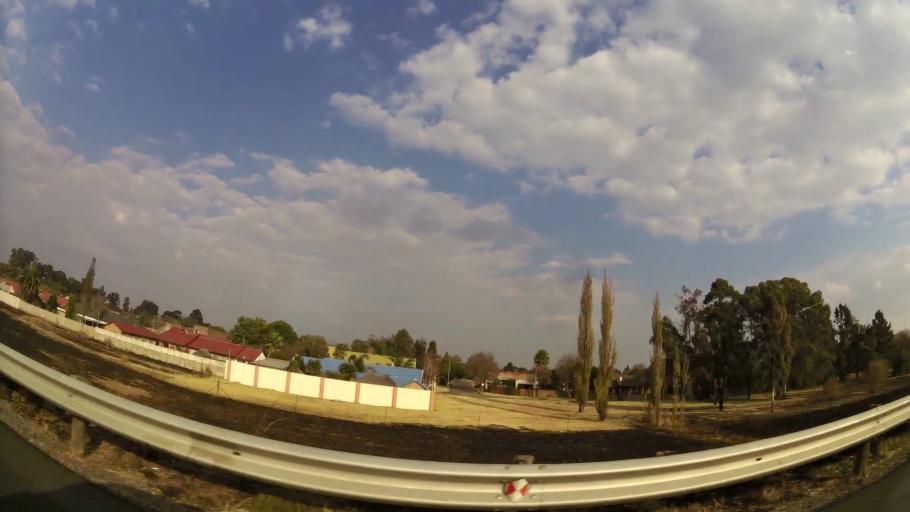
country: ZA
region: Gauteng
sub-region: Ekurhuleni Metropolitan Municipality
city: Springs
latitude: -26.2758
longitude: 28.4632
